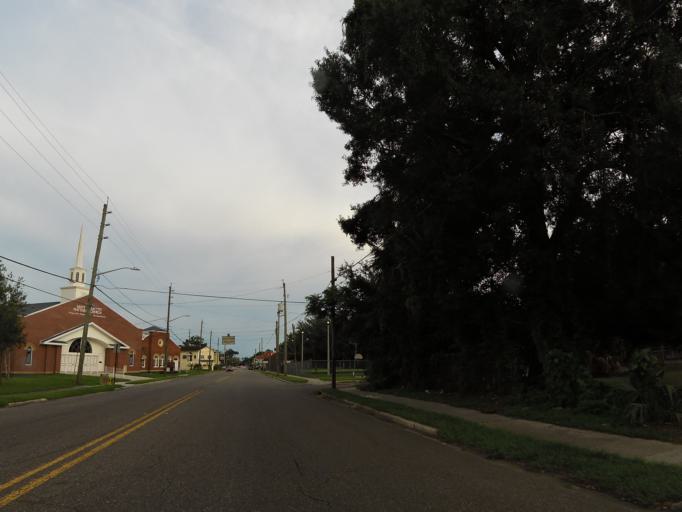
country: US
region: Florida
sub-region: Duval County
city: Jacksonville
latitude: 30.3622
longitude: -81.6777
